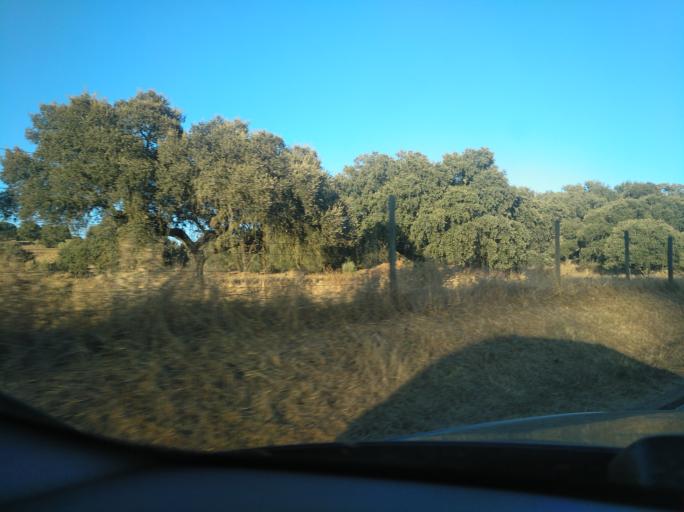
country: PT
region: Portalegre
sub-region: Arronches
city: Arronches
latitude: 39.0709
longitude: -7.2492
